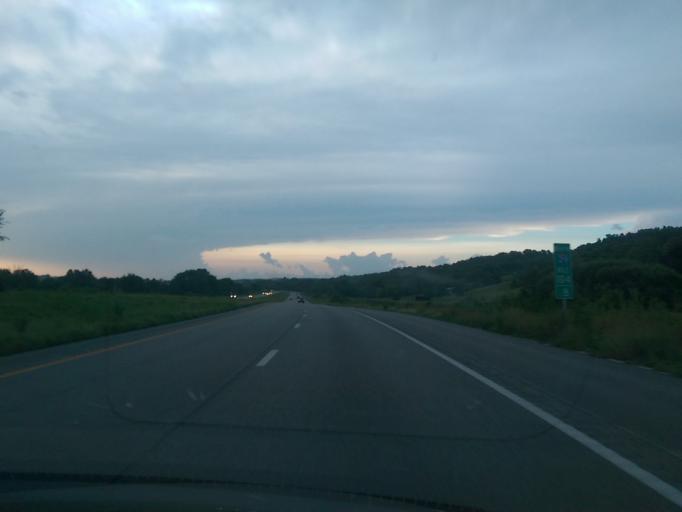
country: US
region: Missouri
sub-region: Atchison County
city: Rock Port
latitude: 40.3340
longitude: -95.4976
